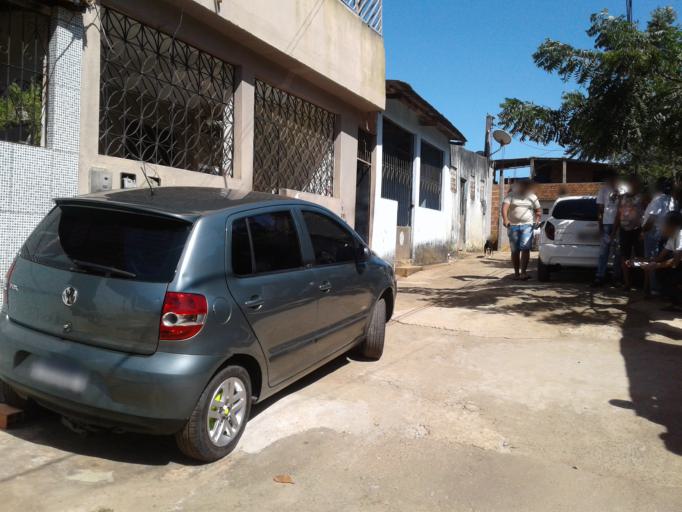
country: BR
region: Bahia
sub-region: Salvador
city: Salvador
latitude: -12.9117
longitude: -38.4674
